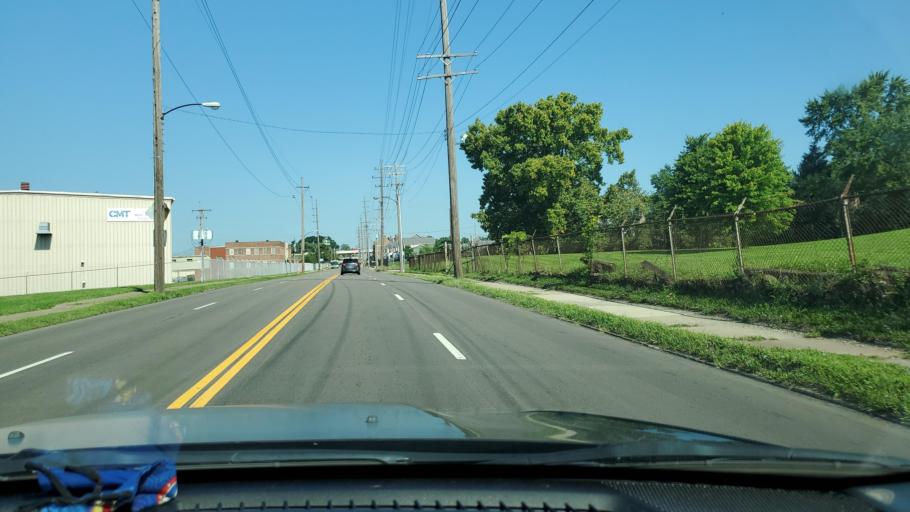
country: US
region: Ohio
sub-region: Mahoning County
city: Youngstown
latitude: 41.1076
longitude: -80.6612
